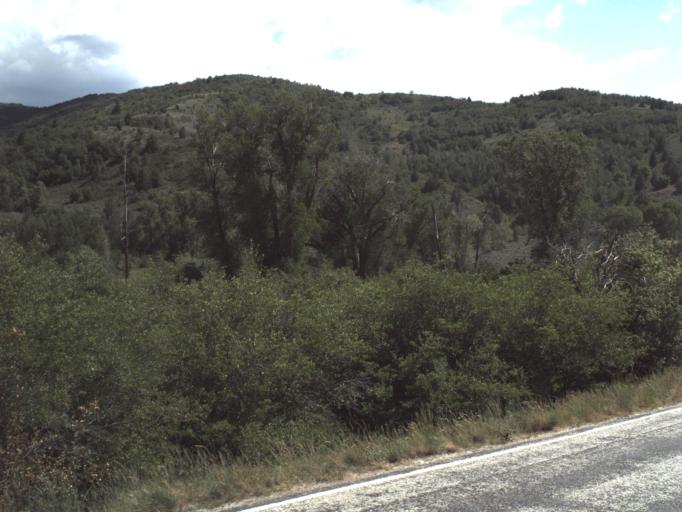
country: US
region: Utah
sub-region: Weber County
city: Wolf Creek
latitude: 41.2885
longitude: -111.6439
